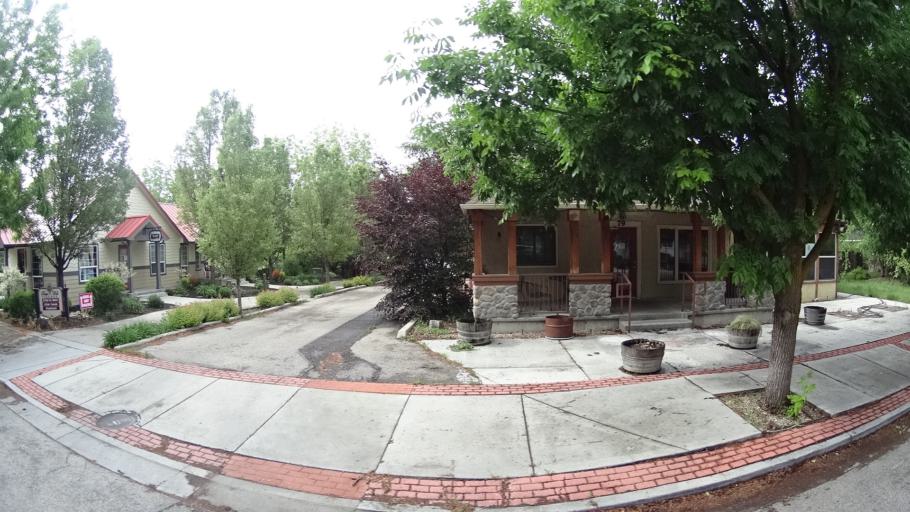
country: US
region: Idaho
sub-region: Ada County
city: Eagle
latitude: 43.6942
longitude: -116.3527
